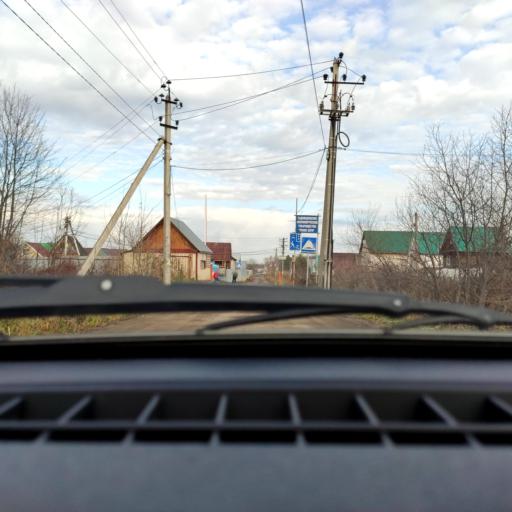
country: RU
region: Bashkortostan
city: Ufa
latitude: 54.6308
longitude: 55.8900
